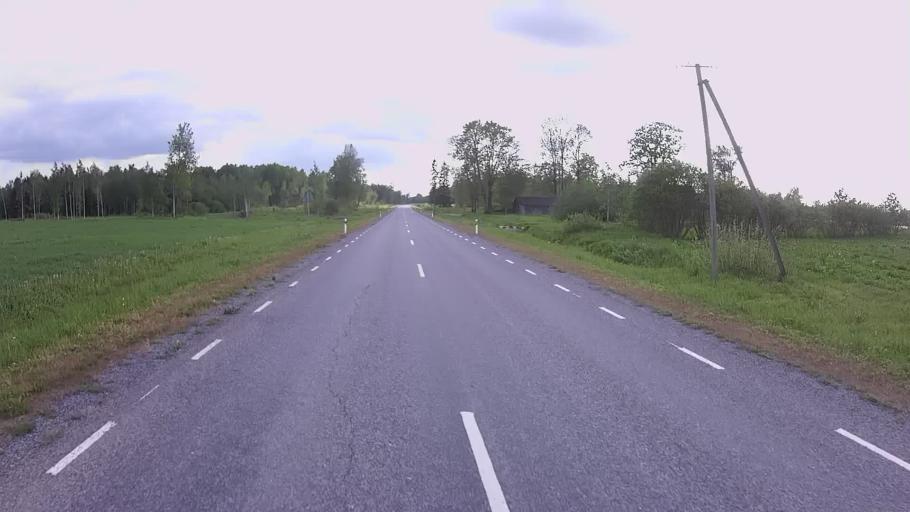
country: EE
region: Jogevamaa
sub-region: Mustvee linn
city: Mustvee
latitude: 59.0158
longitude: 26.9444
